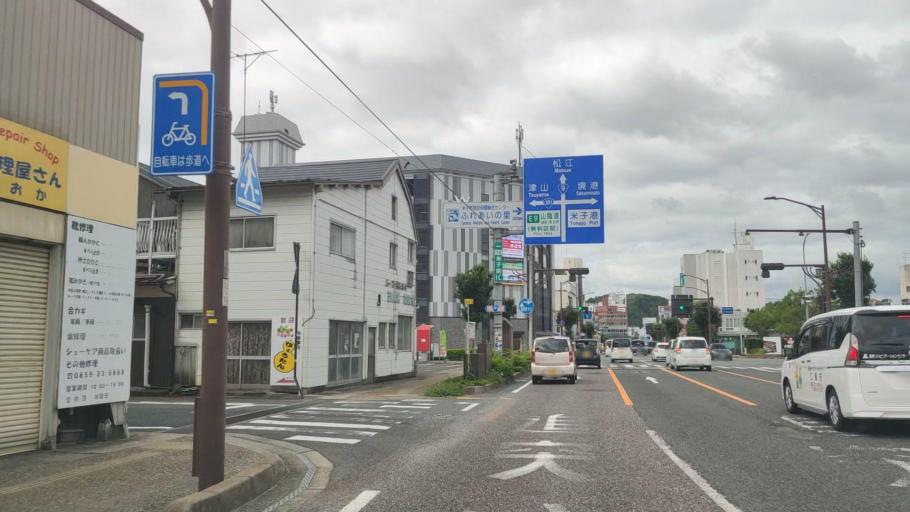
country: JP
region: Tottori
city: Yonago
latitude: 35.4336
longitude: 133.3344
